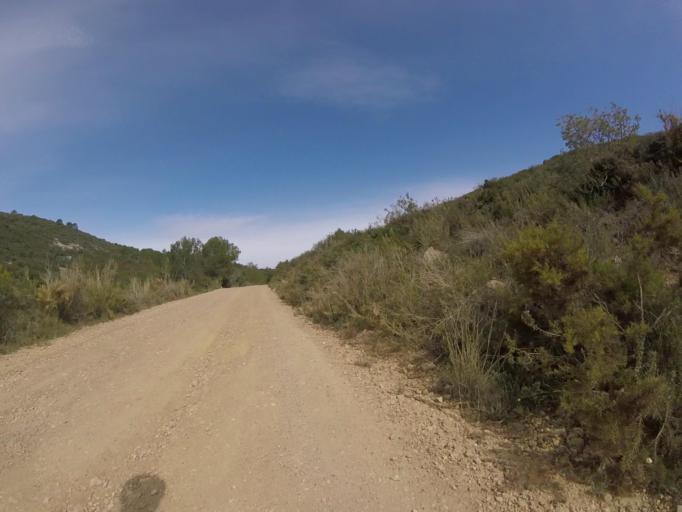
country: ES
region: Valencia
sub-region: Provincia de Castello
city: Torreblanca
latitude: 40.2024
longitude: 0.1516
